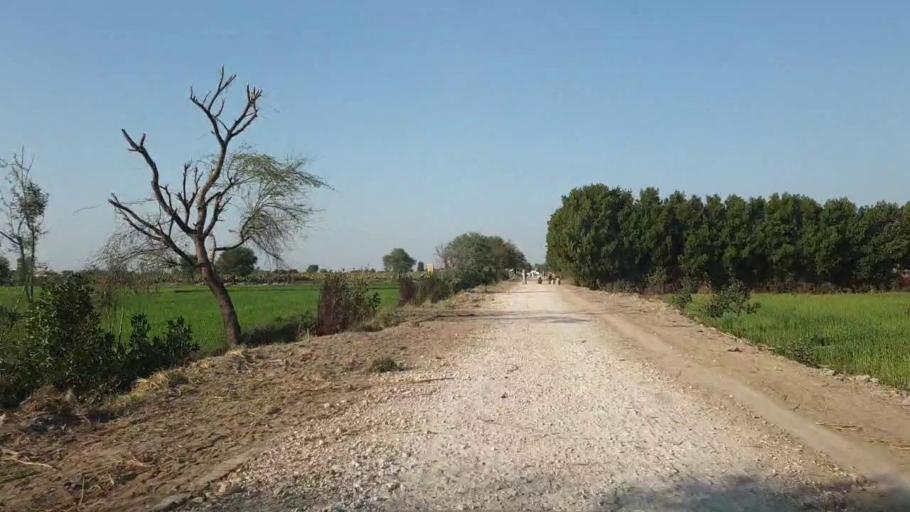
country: PK
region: Sindh
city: Tando Allahyar
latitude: 25.3828
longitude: 68.6841
